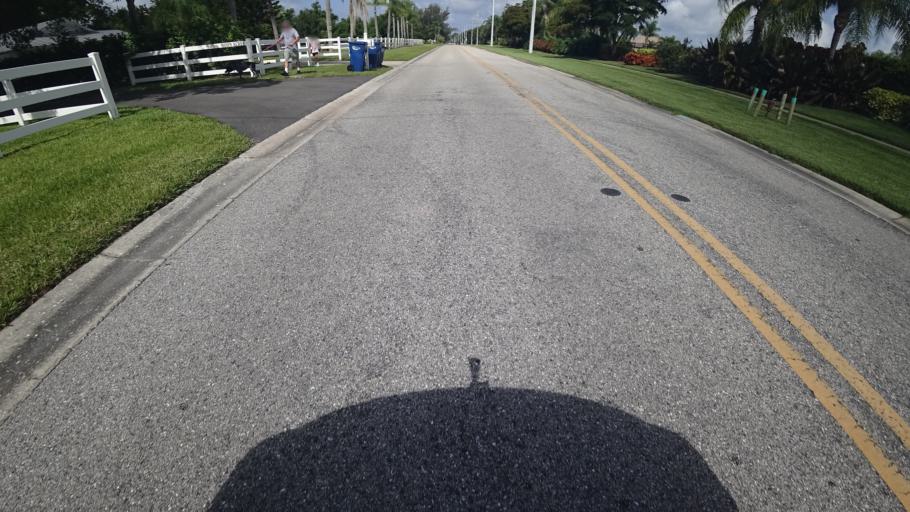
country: US
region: Florida
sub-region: Manatee County
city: West Bradenton
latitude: 27.5145
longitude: -82.6489
